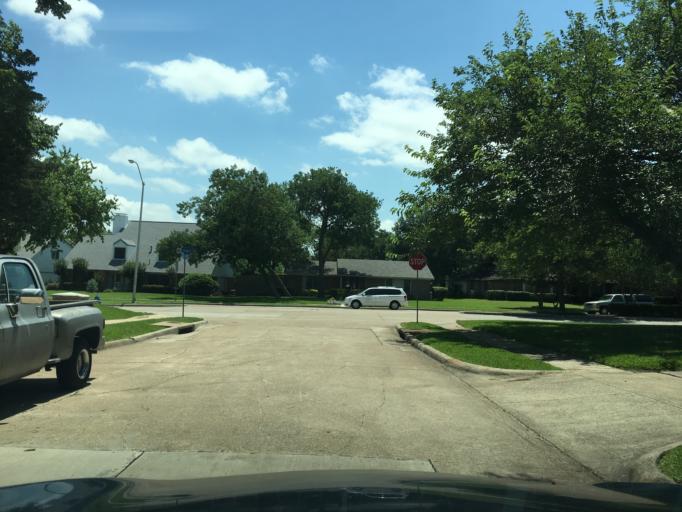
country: US
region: Texas
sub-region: Dallas County
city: Richardson
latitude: 32.9688
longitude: -96.6926
